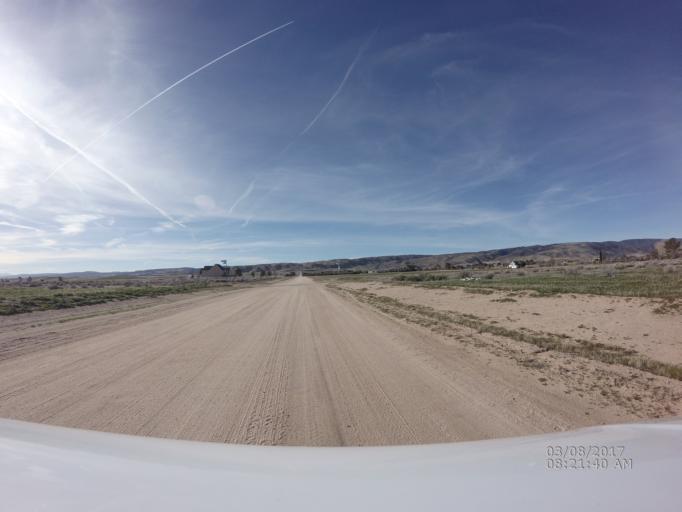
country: US
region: California
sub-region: Los Angeles County
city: Green Valley
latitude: 34.7463
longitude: -118.4489
